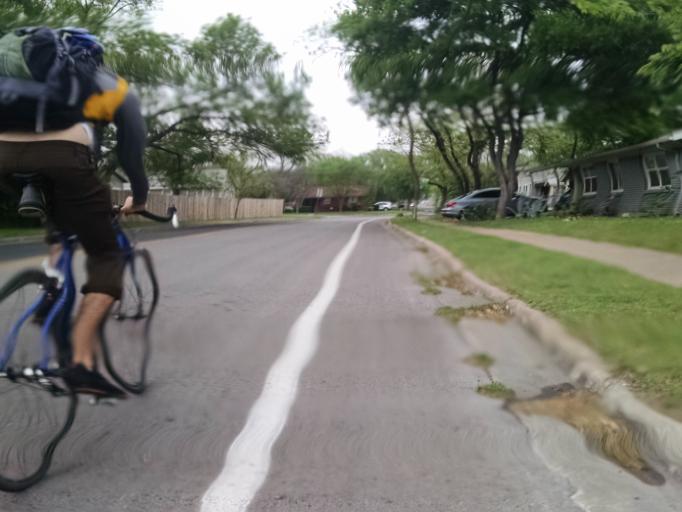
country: US
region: Texas
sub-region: Travis County
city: Austin
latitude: 30.3313
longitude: -97.7189
